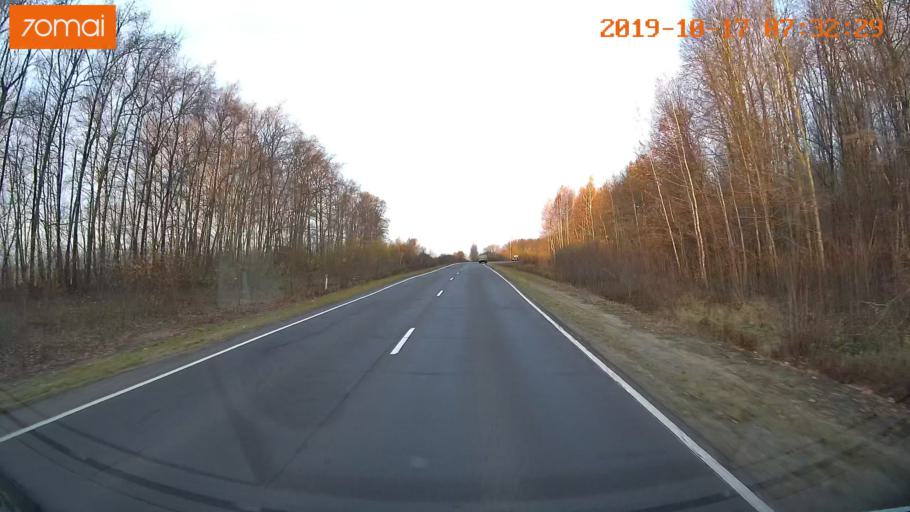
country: RU
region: Ivanovo
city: Gavrilov Posad
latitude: 56.3975
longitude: 39.9741
